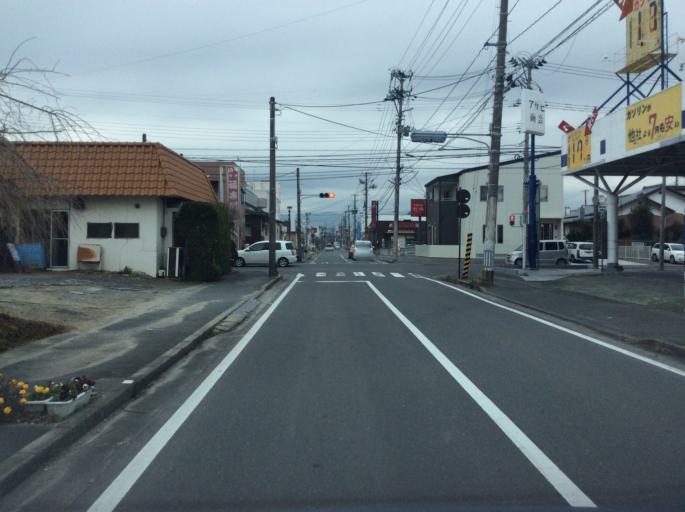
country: JP
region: Fukushima
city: Iwaki
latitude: 37.0493
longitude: 140.9056
